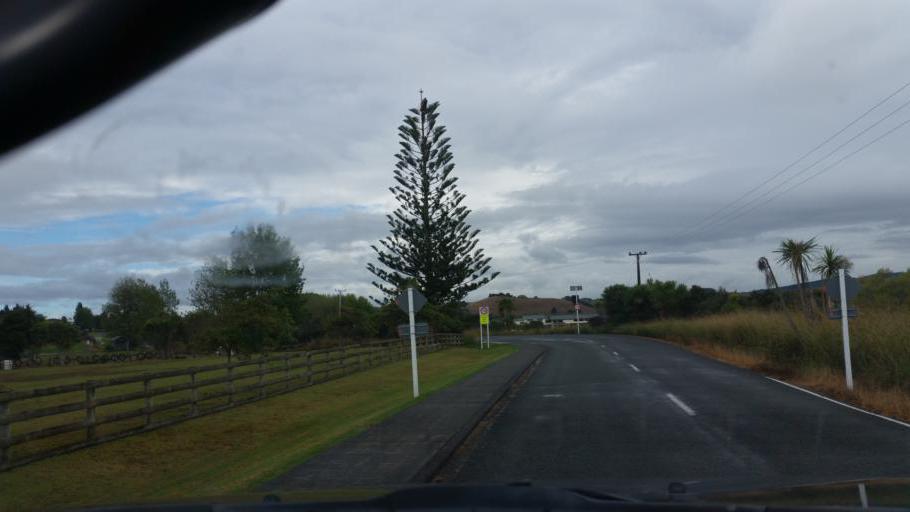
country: NZ
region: Northland
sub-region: Whangarei
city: Ruakaka
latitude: -36.1149
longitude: 174.3654
